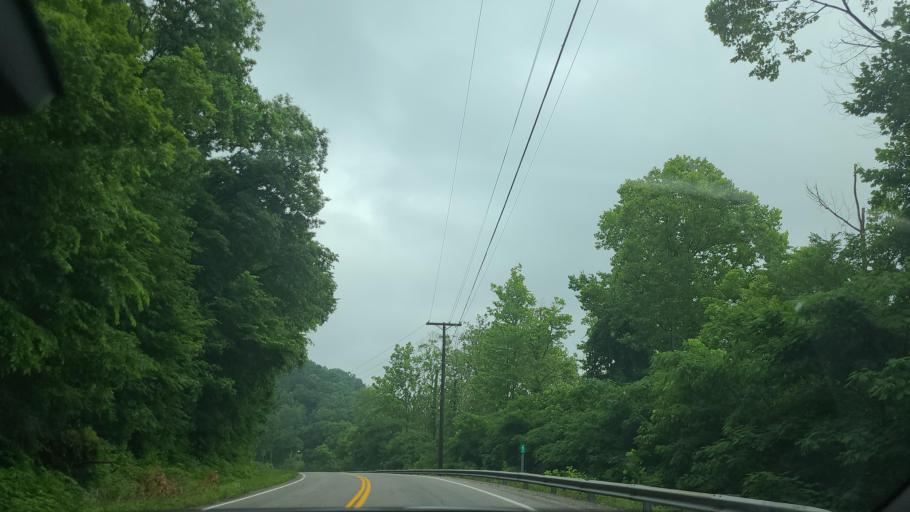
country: US
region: Tennessee
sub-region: Anderson County
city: Oak Ridge
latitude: 36.0913
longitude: -84.2672
